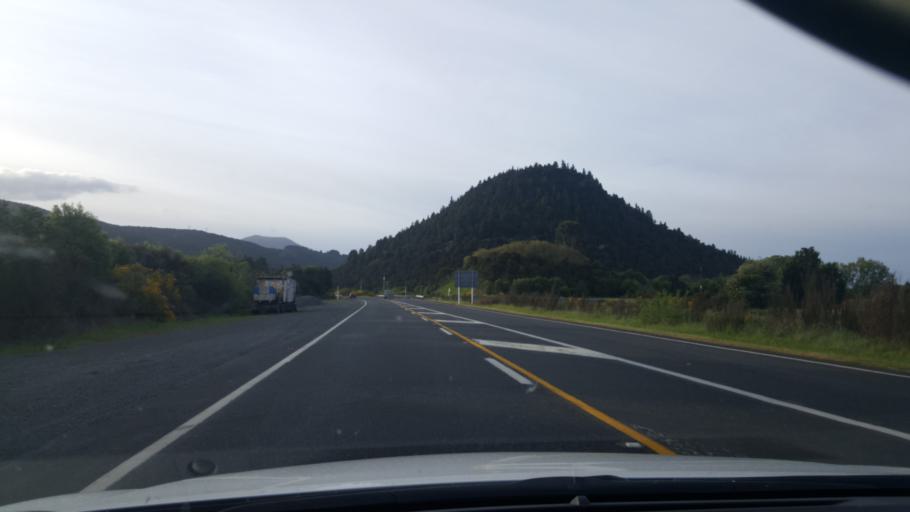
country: NZ
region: Waikato
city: Turangi
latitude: -38.9814
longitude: 175.7791
